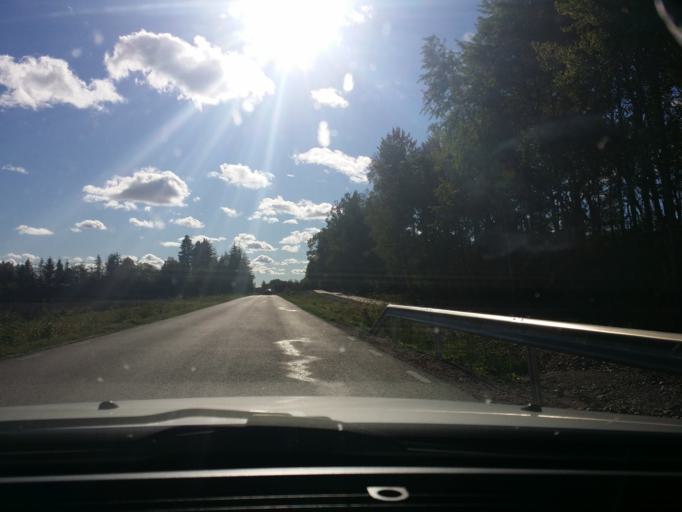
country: SE
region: Vaestmanland
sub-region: Vasteras
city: Vasteras
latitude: 59.5670
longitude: 16.4822
